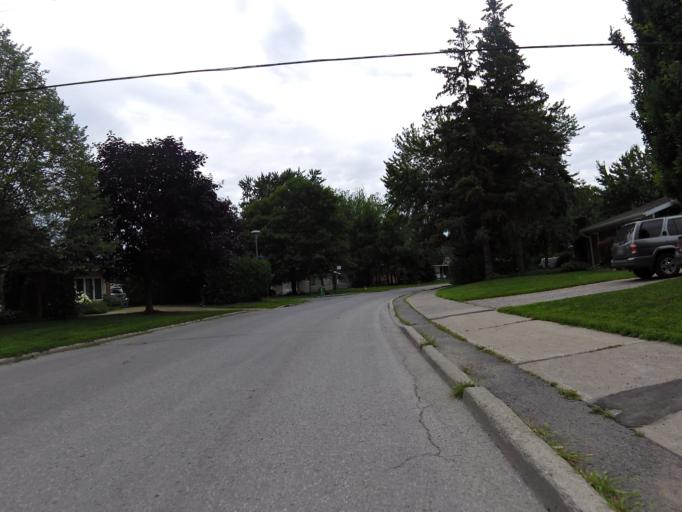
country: CA
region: Ontario
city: Bells Corners
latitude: 45.3477
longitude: -75.8343
